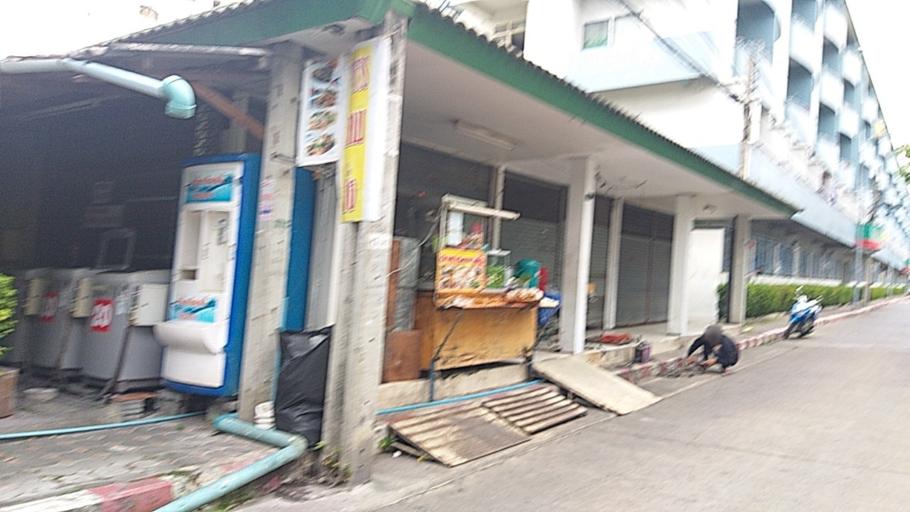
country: TH
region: Bangkok
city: Bang Na
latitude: 13.6693
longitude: 100.6812
